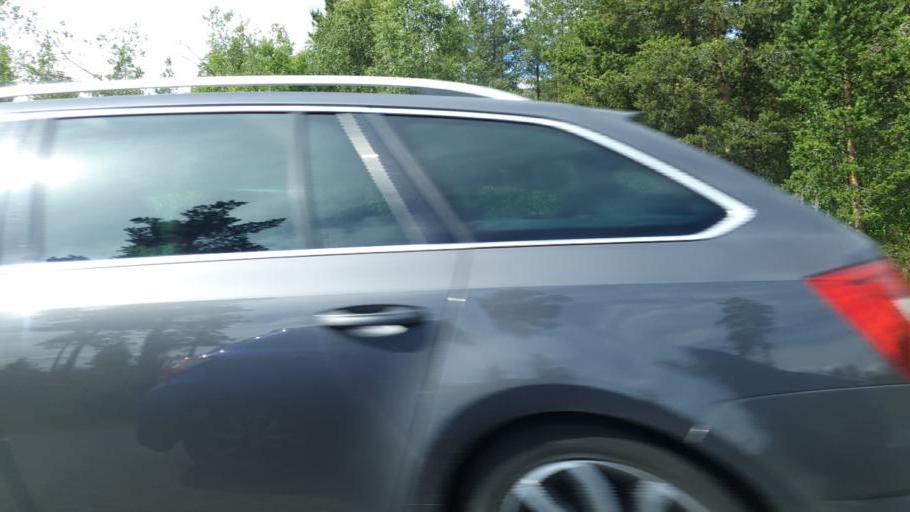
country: NO
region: Oppland
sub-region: Vaga
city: Vagamo
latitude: 61.7353
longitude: 9.0916
